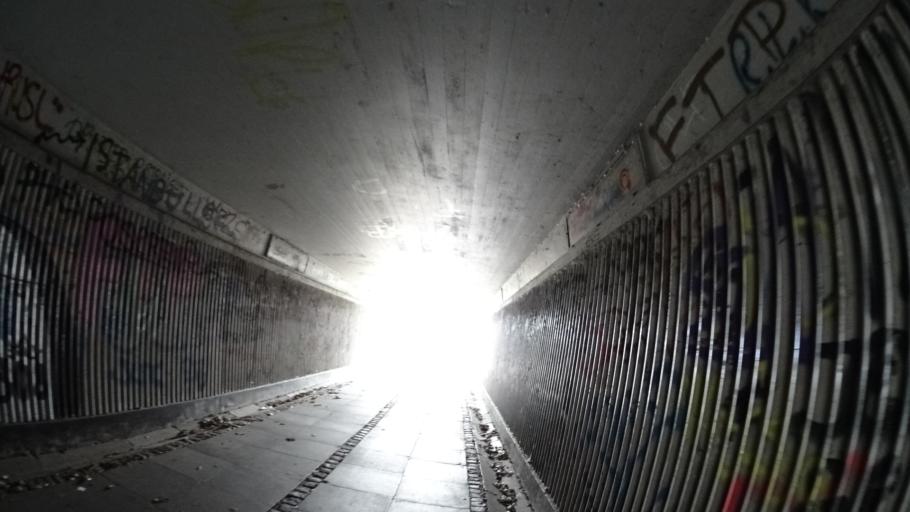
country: DK
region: Central Jutland
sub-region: Arhus Kommune
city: Stavtrup
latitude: 56.1539
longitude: 10.1073
